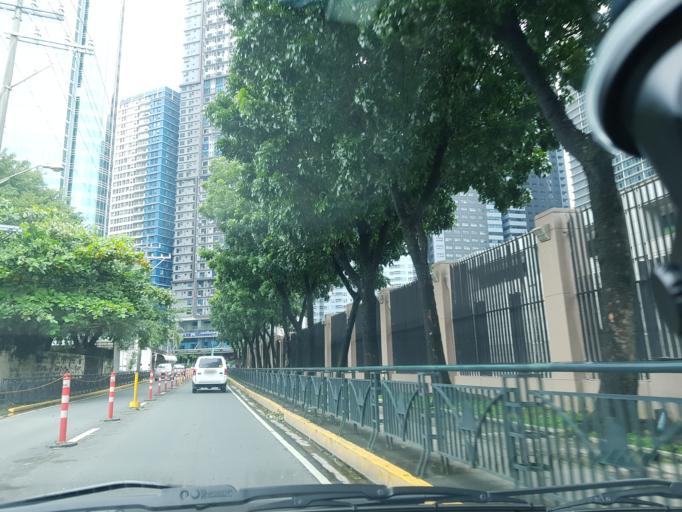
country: PH
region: Metro Manila
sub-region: Pasig
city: Pasig City
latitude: 14.5891
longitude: 121.0585
